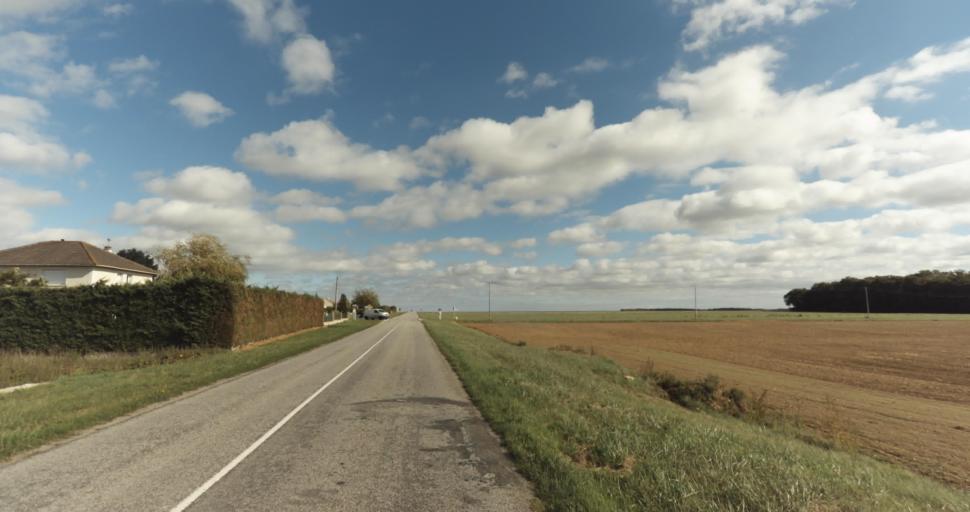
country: FR
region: Centre
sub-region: Departement d'Eure-et-Loir
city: Treon
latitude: 48.6982
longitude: 1.2885
